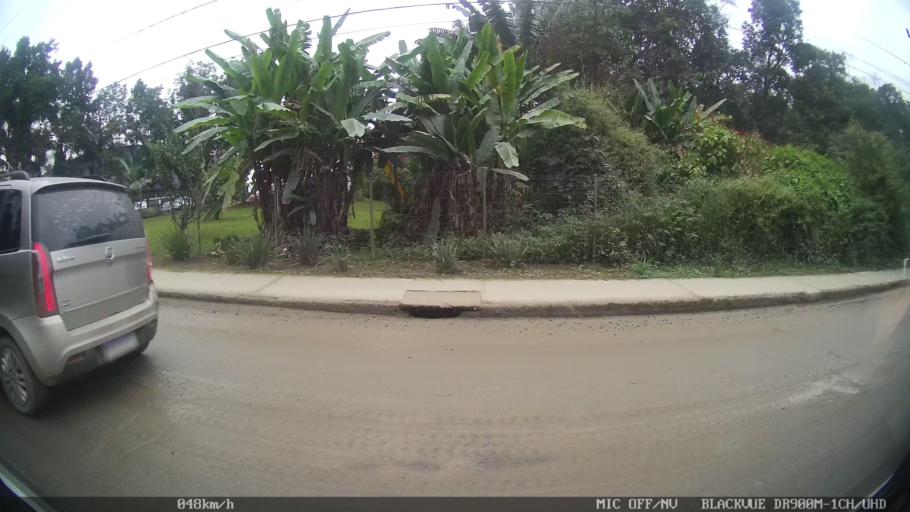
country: BR
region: Santa Catarina
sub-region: Joinville
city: Joinville
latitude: -26.2347
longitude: -48.9261
